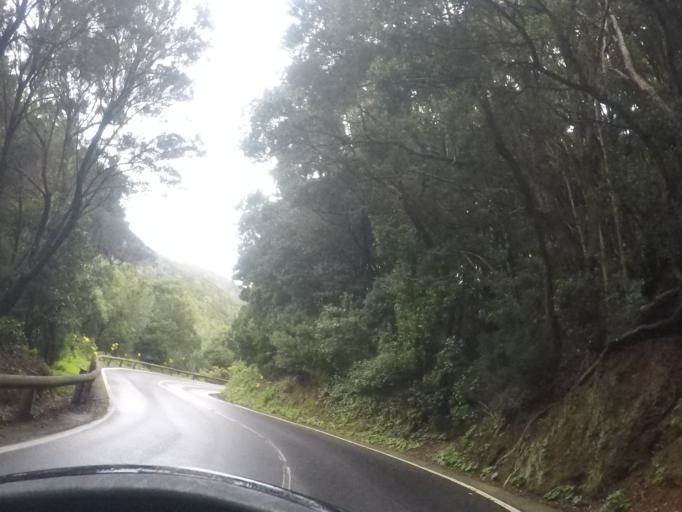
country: ES
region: Canary Islands
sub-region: Provincia de Santa Cruz de Tenerife
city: Tegueste
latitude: 28.5255
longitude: -16.2877
